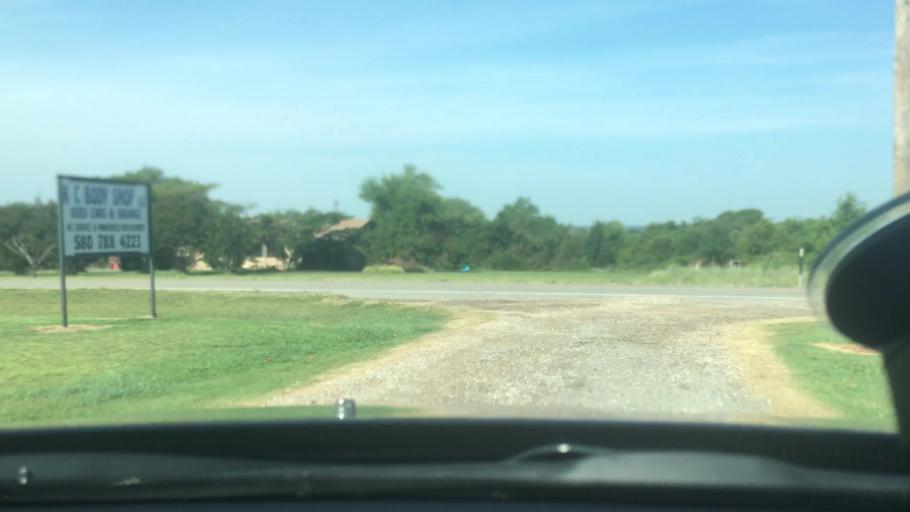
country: US
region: Oklahoma
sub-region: Garvin County
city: Maysville
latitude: 34.6802
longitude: -97.4050
